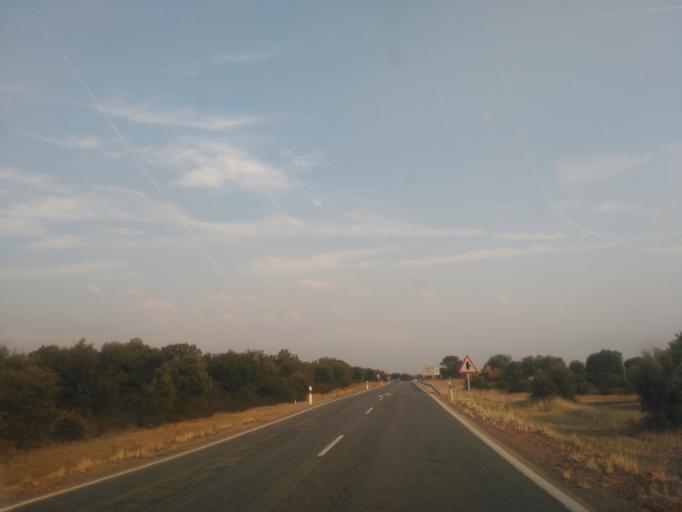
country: ES
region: Castille and Leon
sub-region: Provincia de Zamora
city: Perilla de Castro
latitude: 41.7247
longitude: -5.8153
